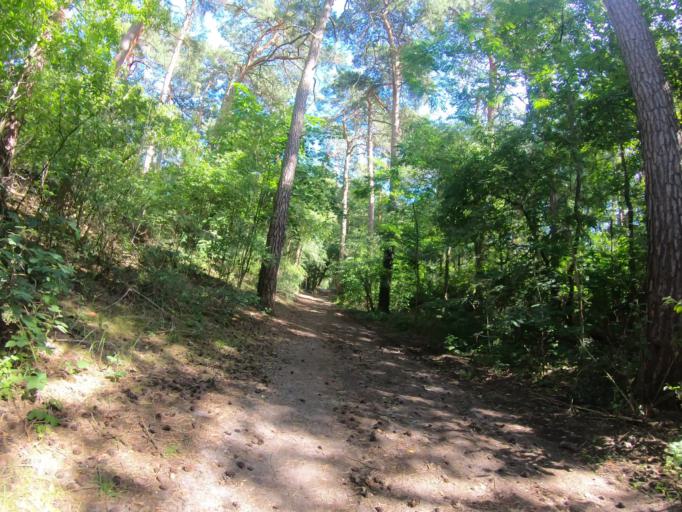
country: DE
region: Lower Saxony
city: Gifhorn
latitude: 52.4801
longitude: 10.5552
